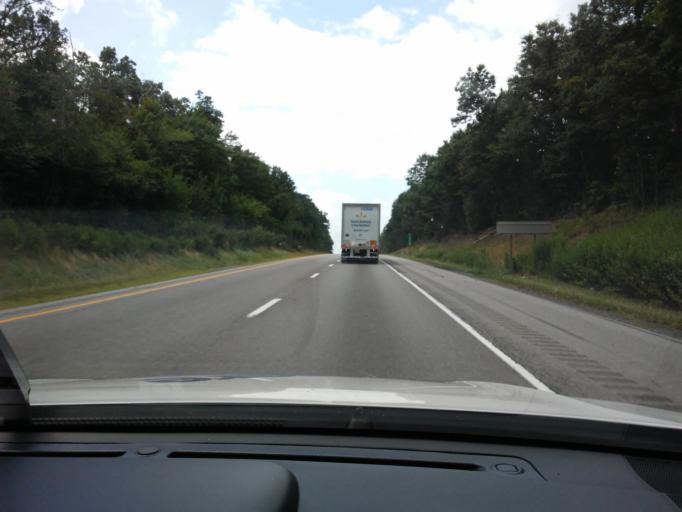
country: US
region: Pennsylvania
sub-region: Centre County
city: Milesburg
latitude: 41.0247
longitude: -77.9223
